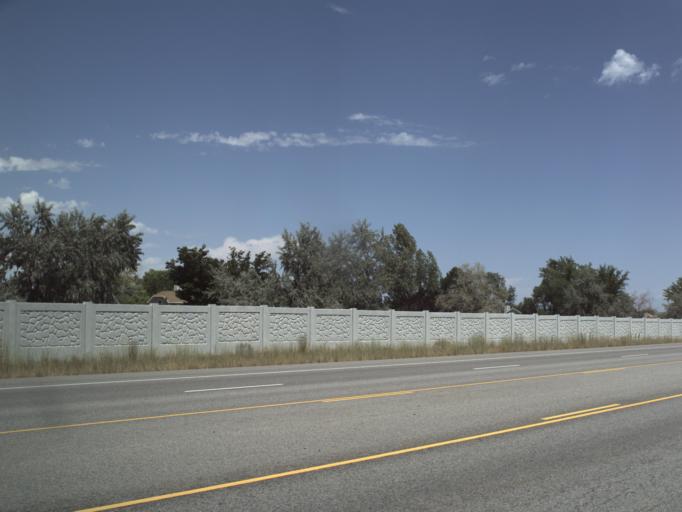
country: US
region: Utah
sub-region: Tooele County
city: Stansbury park
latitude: 40.6367
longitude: -112.2890
